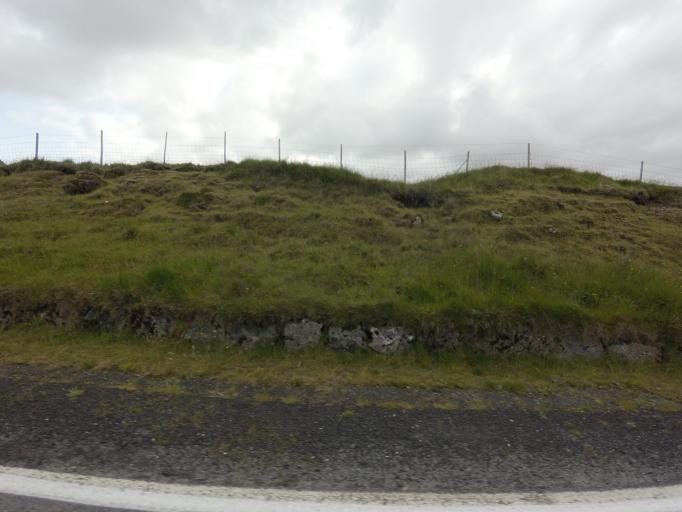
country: FO
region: Eysturoy
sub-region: Eidi
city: Eidi
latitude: 62.2169
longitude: -6.9961
